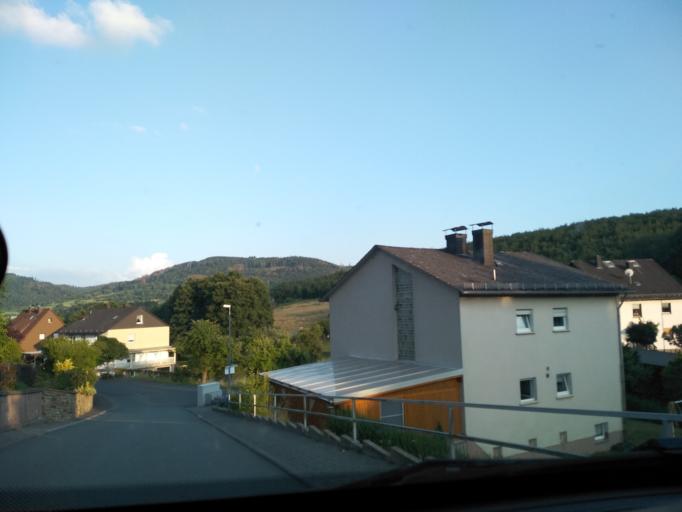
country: DE
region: Hesse
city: Dillenburg
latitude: 50.8109
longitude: 8.3330
